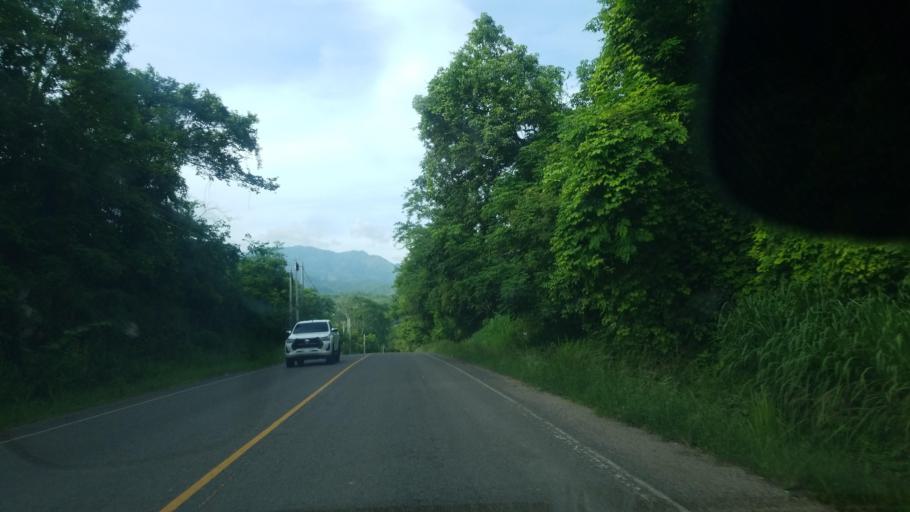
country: HN
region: Santa Barbara
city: Trinidad
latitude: 15.1345
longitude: -88.2474
